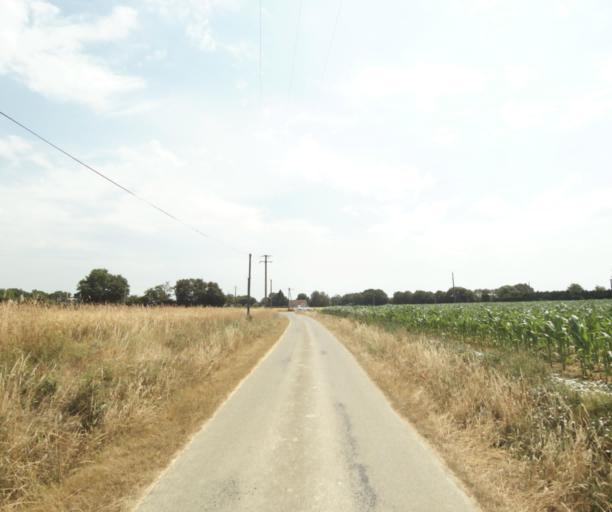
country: FR
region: Centre
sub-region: Departement d'Eure-et-Loir
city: La Bazoche-Gouet
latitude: 48.1834
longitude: 1.0087
